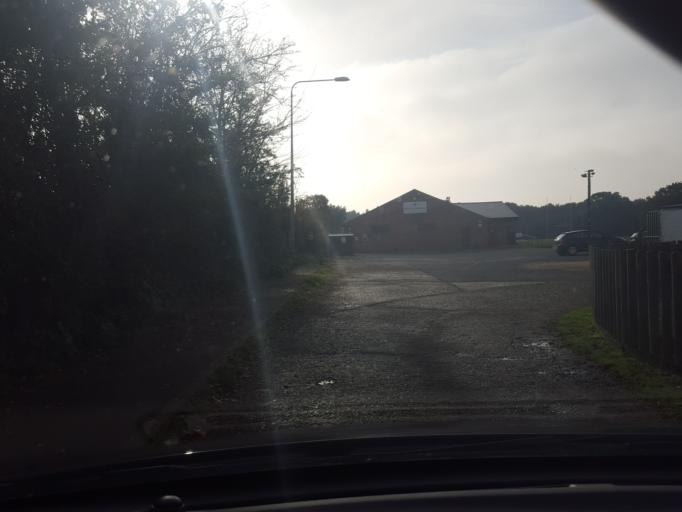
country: GB
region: England
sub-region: Essex
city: Mistley
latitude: 51.9400
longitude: 1.0860
